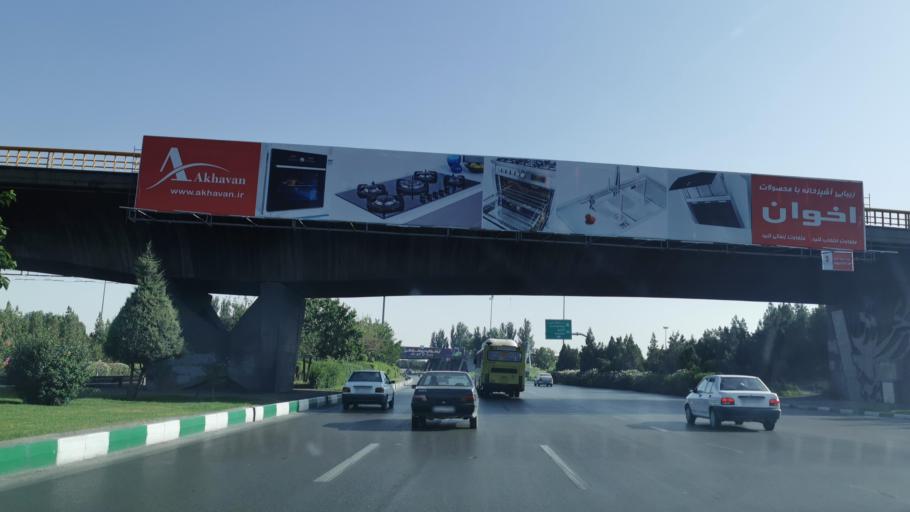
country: IR
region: Razavi Khorasan
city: Mashhad
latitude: 36.3428
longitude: 59.5479
